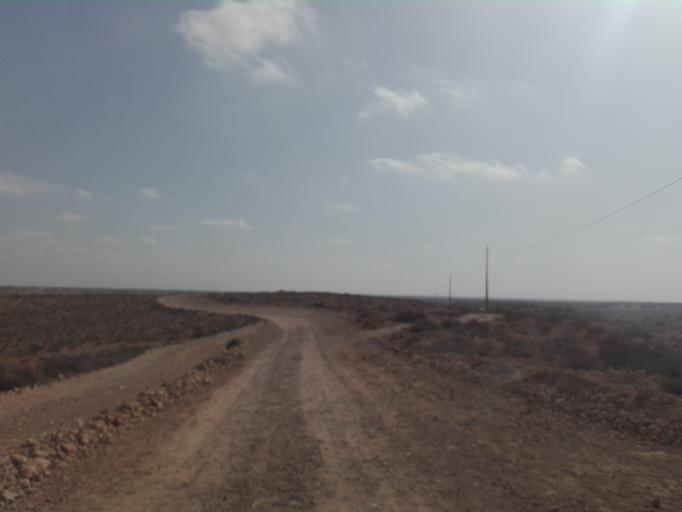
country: TN
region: Madanin
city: Medenine
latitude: 33.4314
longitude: 10.4097
